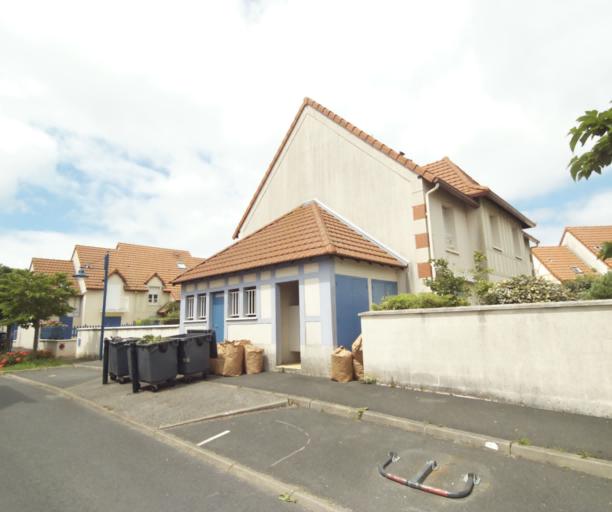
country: FR
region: Lower Normandy
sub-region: Departement du Calvados
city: Dives-sur-Mer
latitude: 49.2948
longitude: -0.0963
